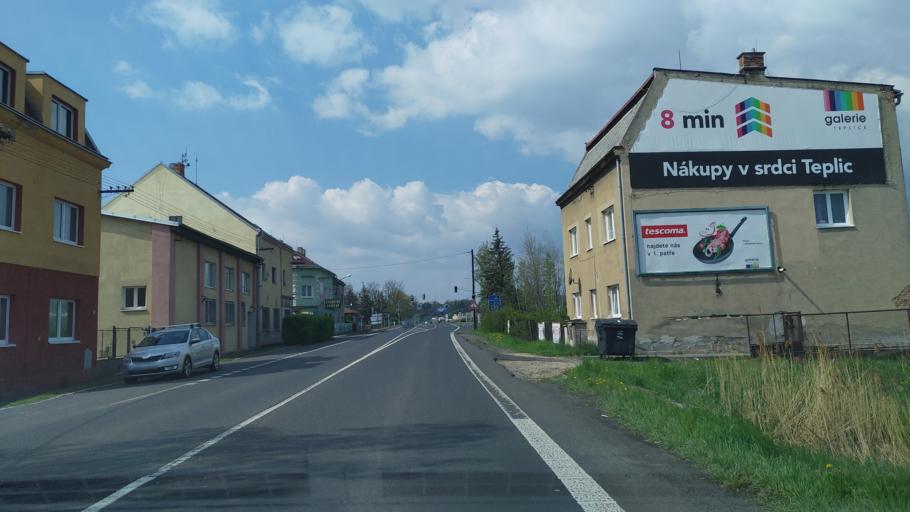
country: CZ
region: Ustecky
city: Krupka
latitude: 50.6611
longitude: 13.8700
